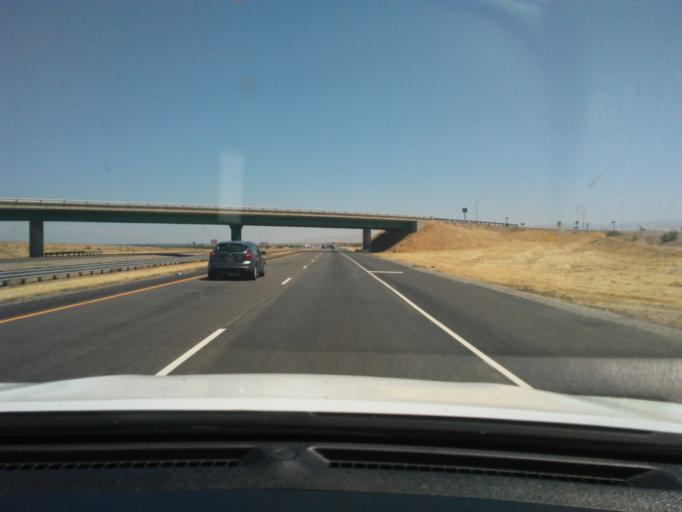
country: US
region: California
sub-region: Fresno County
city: Firebaugh
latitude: 36.6866
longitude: -120.6591
